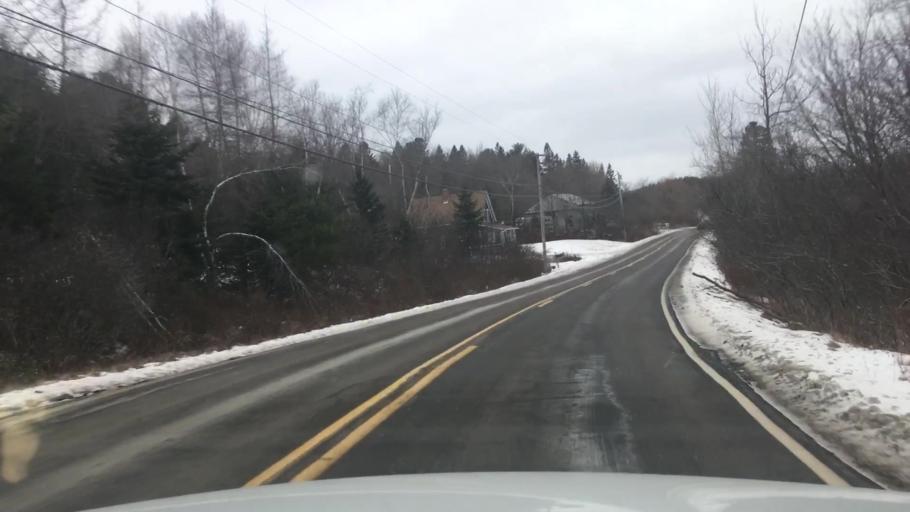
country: US
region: Maine
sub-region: Washington County
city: East Machias
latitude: 44.7270
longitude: -67.3883
